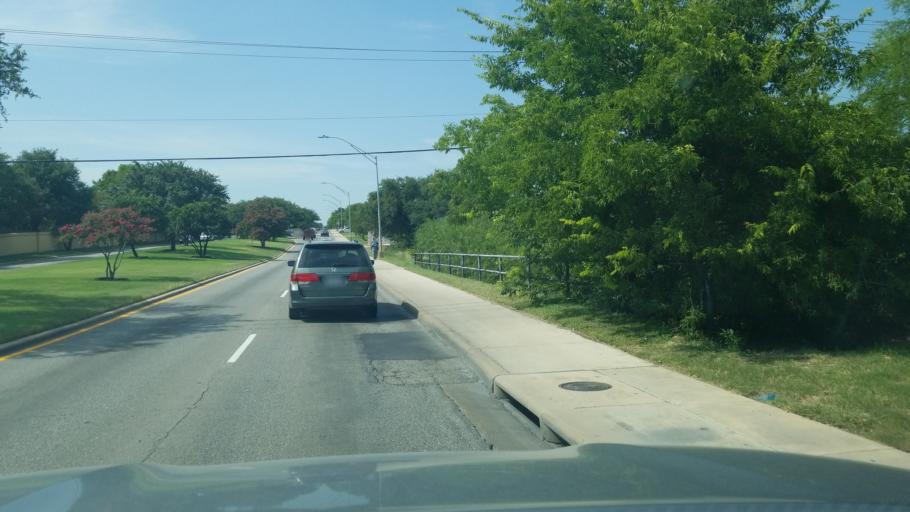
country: US
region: Texas
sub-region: Bexar County
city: Hollywood Park
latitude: 29.6215
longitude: -98.4944
